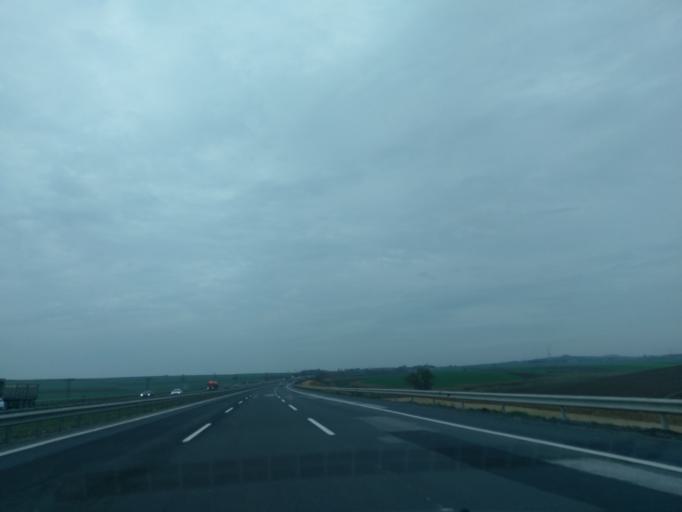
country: TR
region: Istanbul
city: Canta
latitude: 41.1259
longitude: 28.1650
